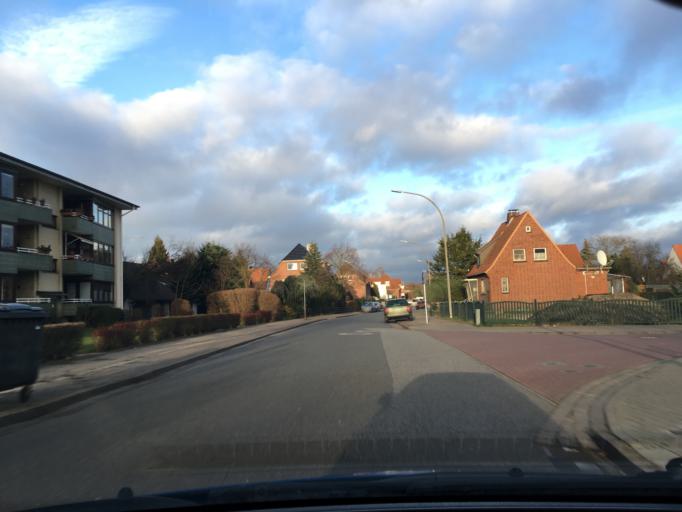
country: DE
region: Lower Saxony
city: Winsen
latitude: 53.3583
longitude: 10.2120
